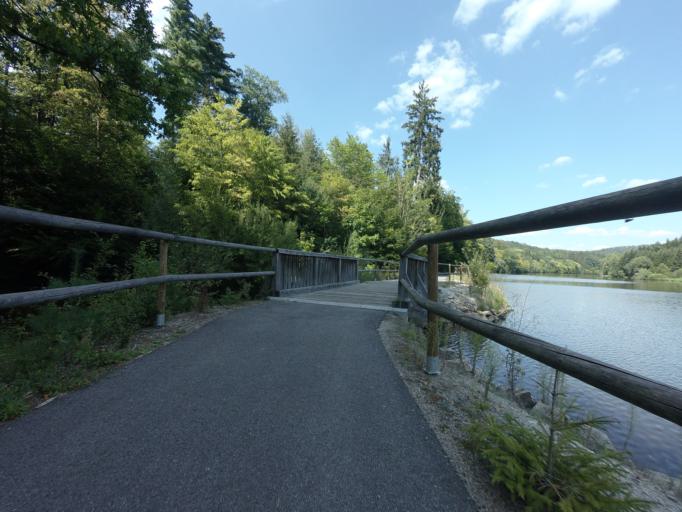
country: CZ
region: Jihocesky
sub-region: Okres Ceske Budejovice
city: Hluboka nad Vltavou
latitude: 49.0777
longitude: 14.4542
